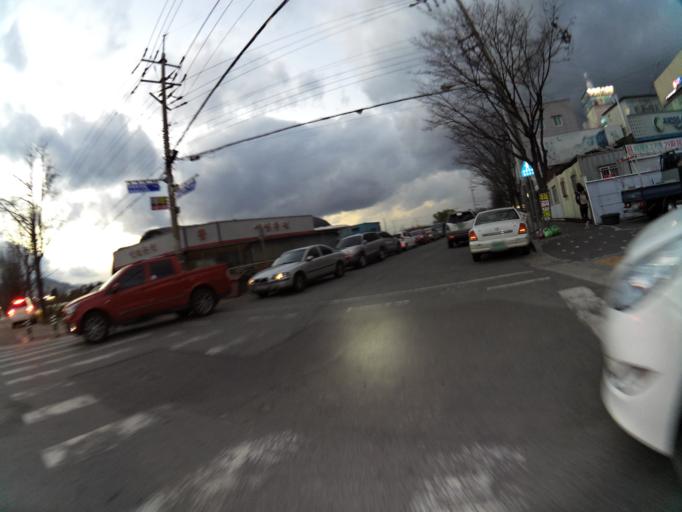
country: KR
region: Gyeongsangbuk-do
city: Gyeongsan-si
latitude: 35.8359
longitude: 128.7518
